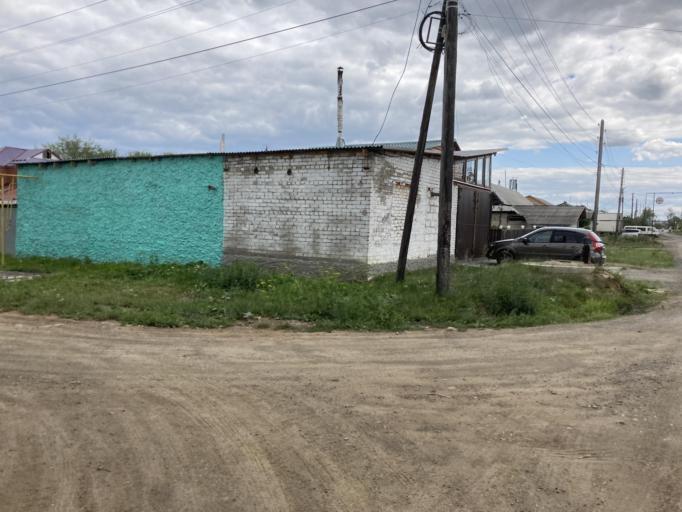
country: RU
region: Sverdlovsk
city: Bogdanovich
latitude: 56.7903
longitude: 62.0501
